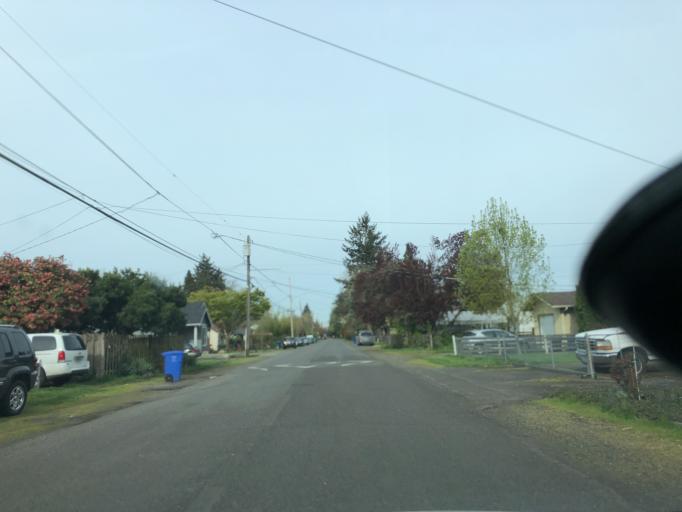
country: US
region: Oregon
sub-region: Multnomah County
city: Portland
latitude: 45.5591
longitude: -122.6102
